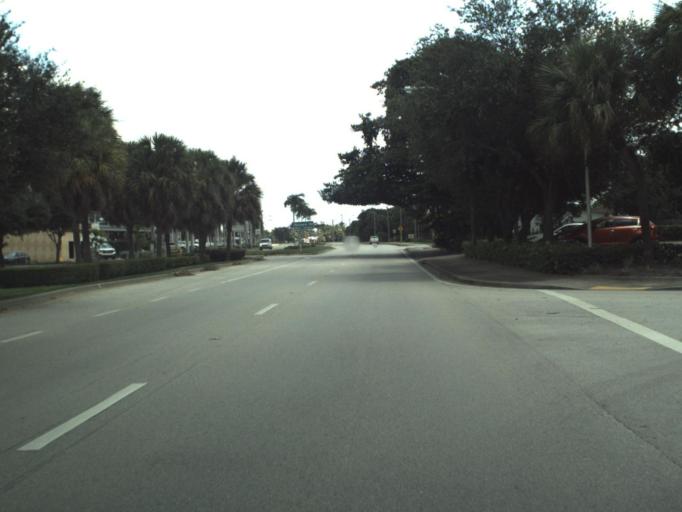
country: US
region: Florida
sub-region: Palm Beach County
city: North Palm Beach
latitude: 26.8102
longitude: -80.0768
